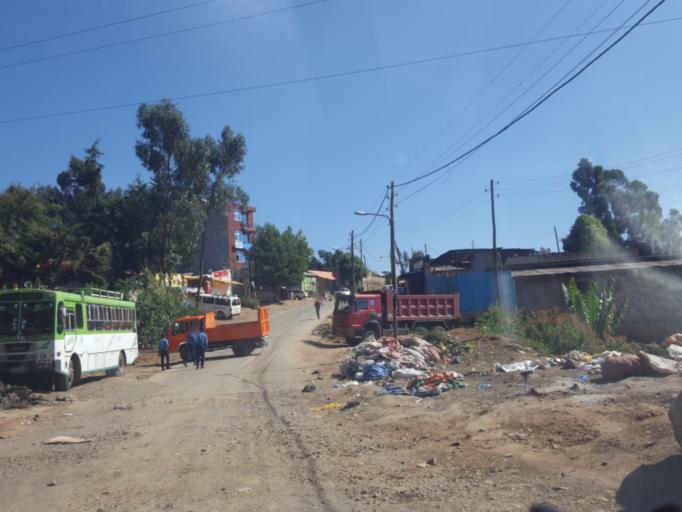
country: ET
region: Adis Abeba
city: Addis Ababa
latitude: 9.0640
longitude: 38.7450
